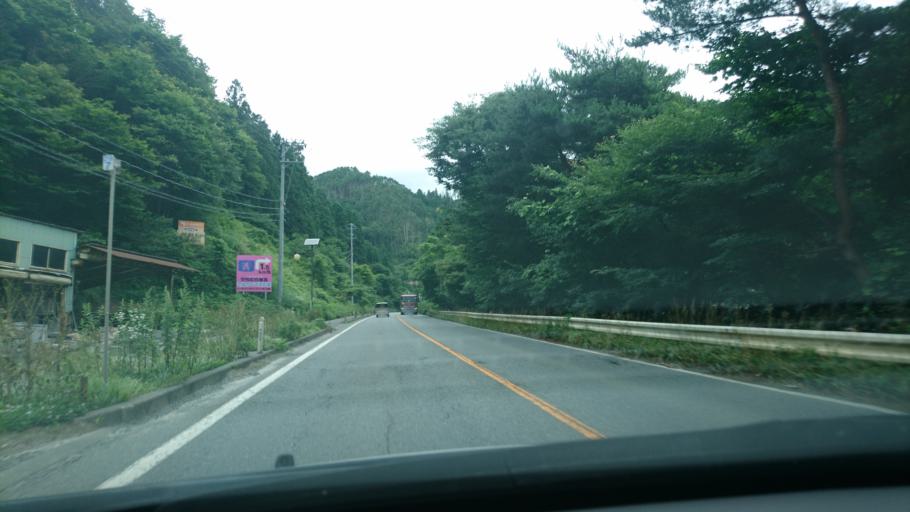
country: JP
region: Iwate
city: Otsuchi
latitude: 39.3413
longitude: 141.8936
